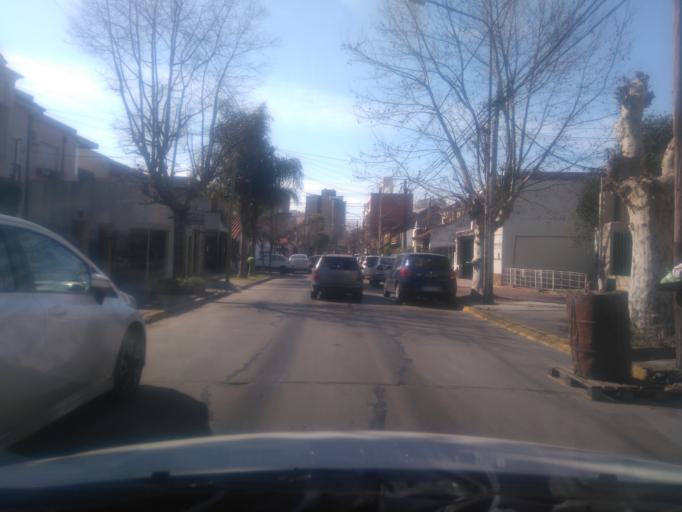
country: AR
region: Buenos Aires
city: San Justo
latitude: -34.6419
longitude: -58.5569
